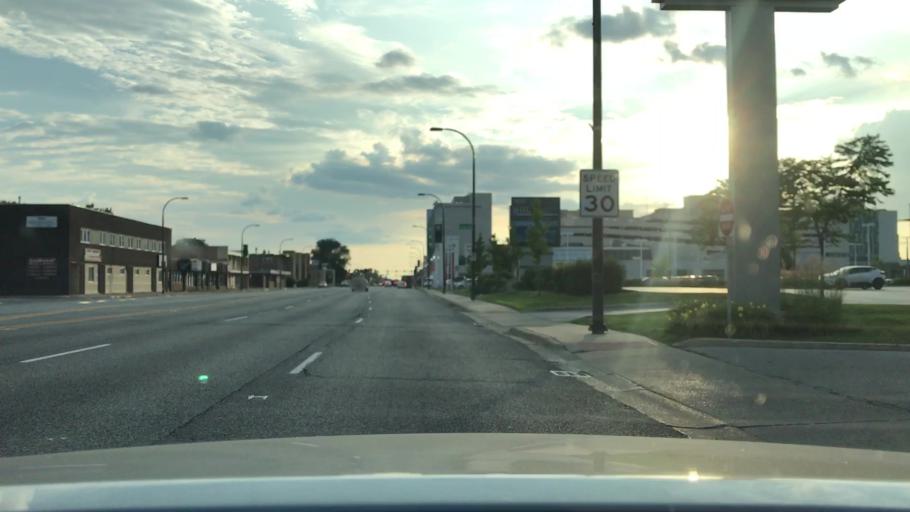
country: US
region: Illinois
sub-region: Cook County
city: Hometown
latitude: 41.7205
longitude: -87.7267
